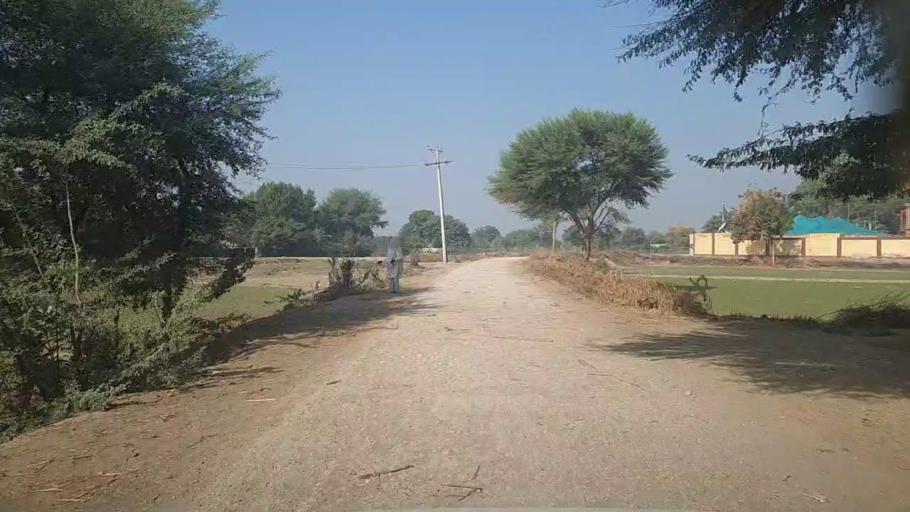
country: PK
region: Sindh
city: Kandiari
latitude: 26.9700
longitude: 68.4555
